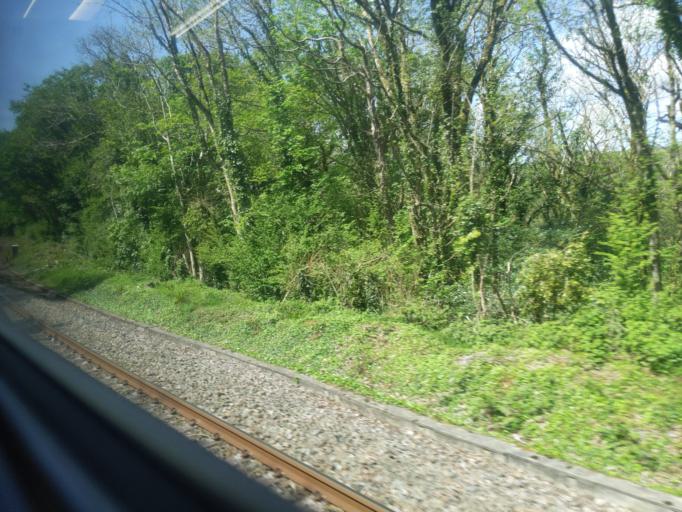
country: GB
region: England
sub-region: Cornwall
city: Liskeard
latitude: 50.4527
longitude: -4.5607
